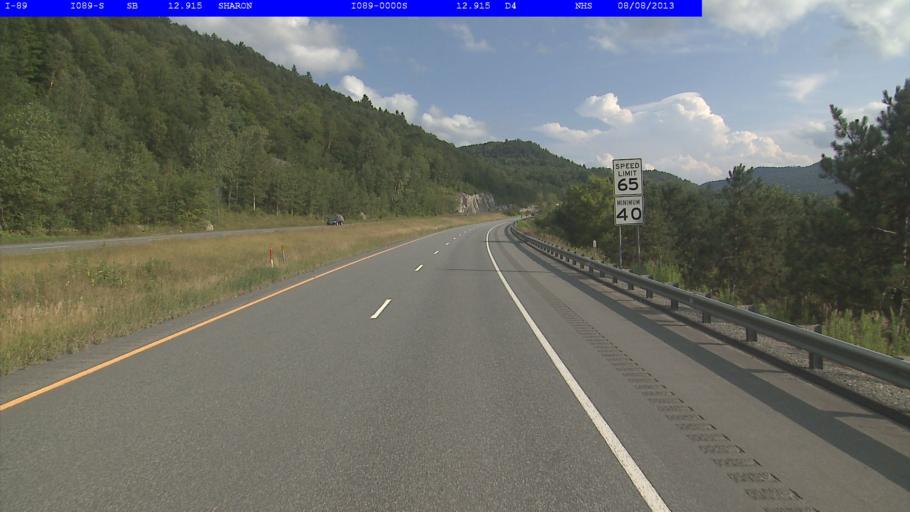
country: US
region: Vermont
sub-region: Windsor County
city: Woodstock
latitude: 43.7813
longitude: -72.4459
